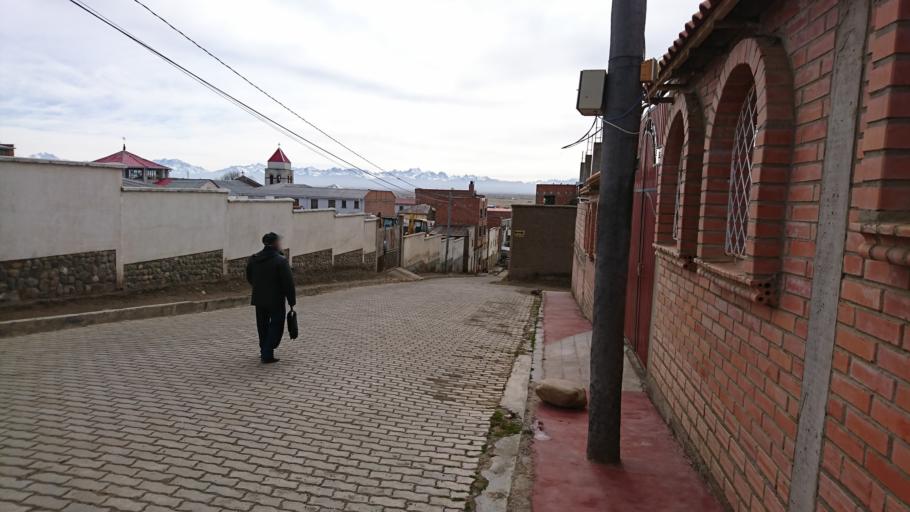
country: BO
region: La Paz
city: Batallas
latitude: -16.4010
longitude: -68.4786
